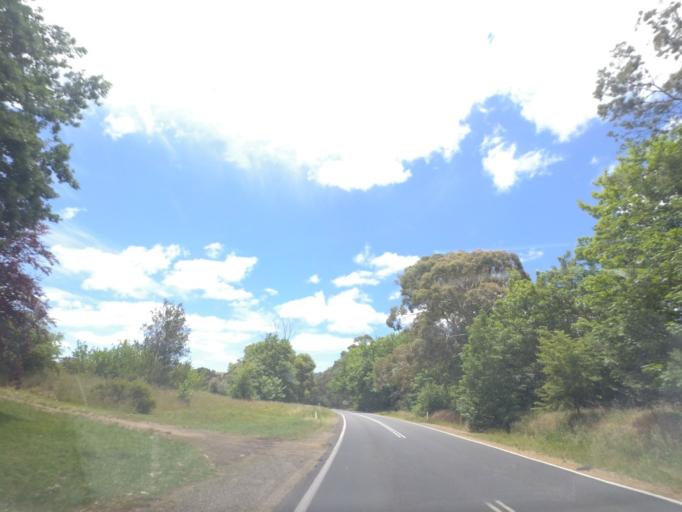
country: AU
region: Victoria
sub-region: Mount Alexander
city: Castlemaine
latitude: -37.3339
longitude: 144.1662
